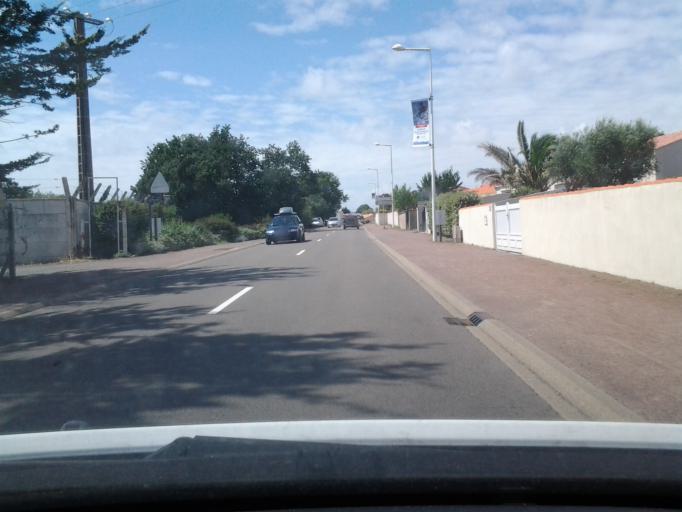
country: FR
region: Pays de la Loire
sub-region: Departement de la Vendee
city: Olonne-sur-Mer
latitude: 46.5330
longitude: -1.7600
